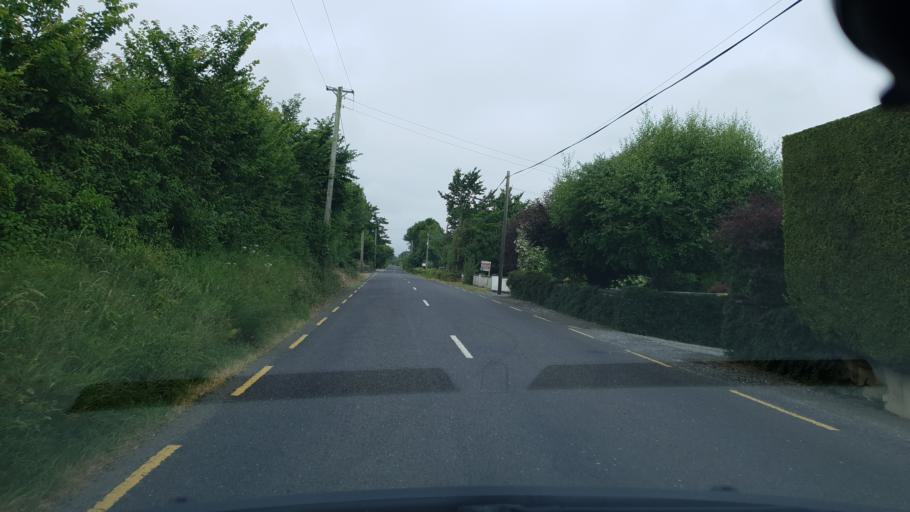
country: IE
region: Munster
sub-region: Ciarrai
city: Tralee
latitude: 52.1636
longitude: -9.6193
